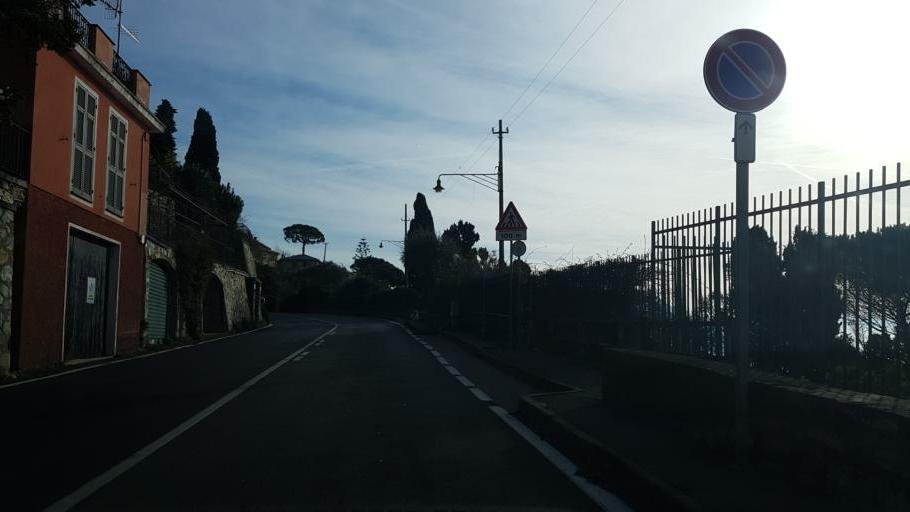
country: IT
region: Liguria
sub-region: Provincia di Genova
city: Sori
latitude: 44.3694
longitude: 9.1083
